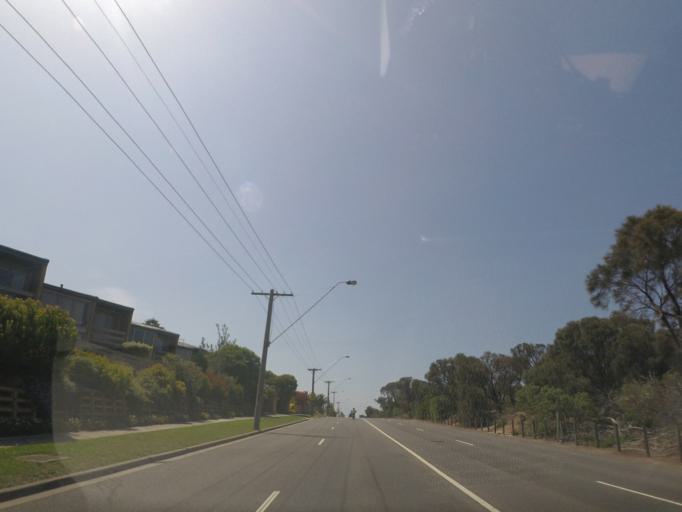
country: AU
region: Victoria
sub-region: Kingston
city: Mentone
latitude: -37.9894
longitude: 145.0609
